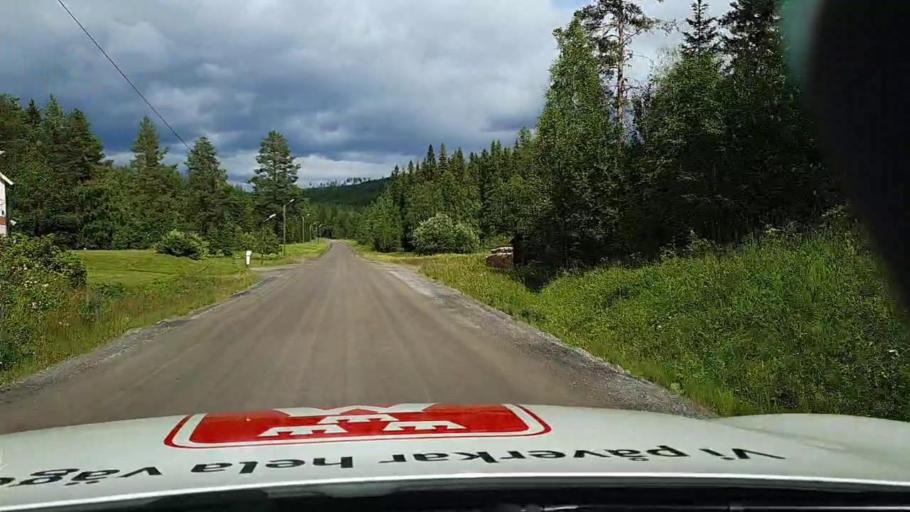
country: SE
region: Vaesternorrland
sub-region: Solleftea Kommun
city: As
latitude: 63.4646
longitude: 16.2753
